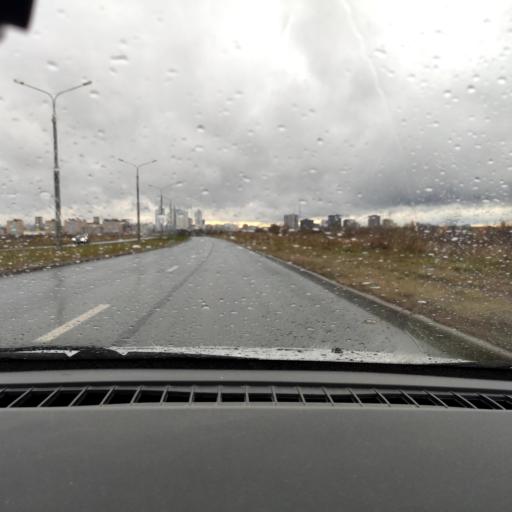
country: RU
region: Perm
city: Perm
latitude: 58.0068
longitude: 56.3540
